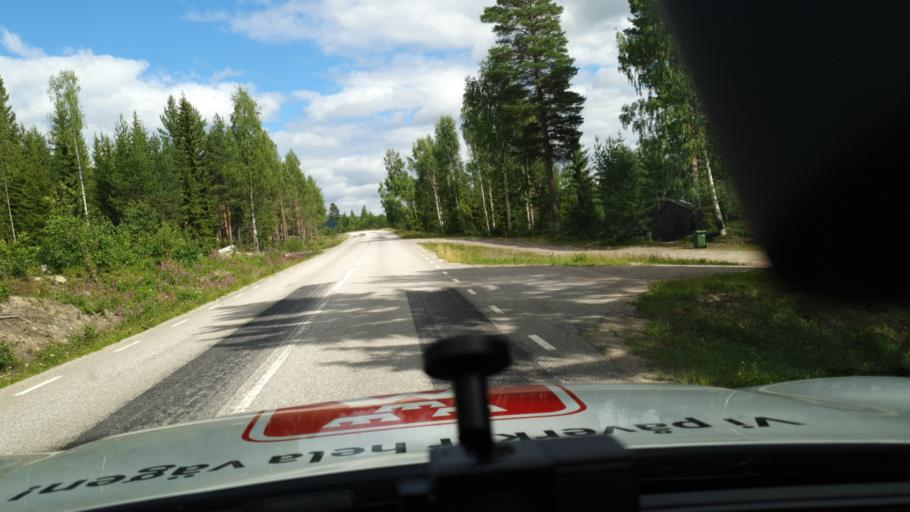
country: NO
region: Hedmark
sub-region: Trysil
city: Innbygda
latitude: 61.0295
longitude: 12.5712
